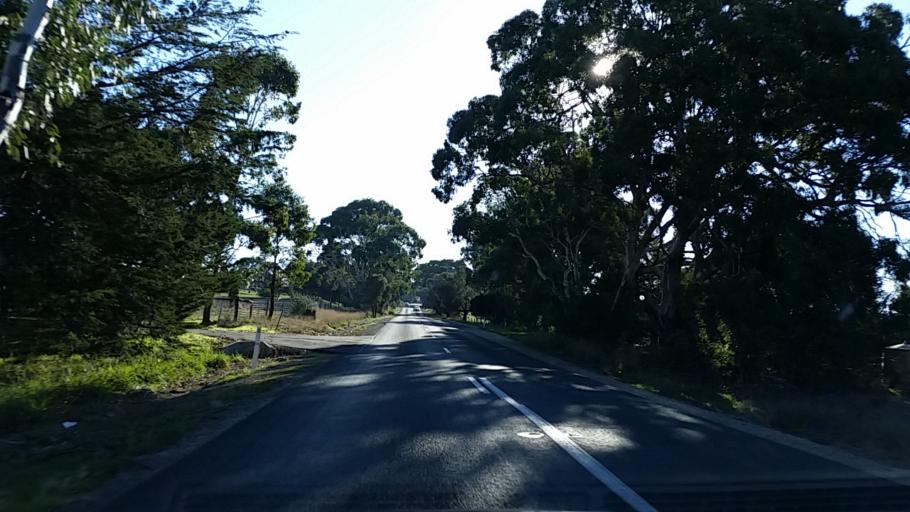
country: AU
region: South Australia
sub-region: Mount Barker
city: Macclesfield
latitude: -35.1460
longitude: 138.9276
